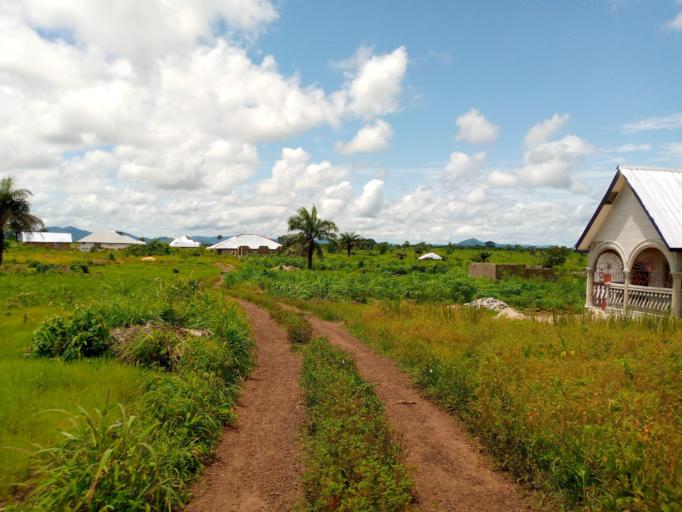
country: SL
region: Northern Province
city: Magburaka
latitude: 8.7184
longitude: -11.9241
